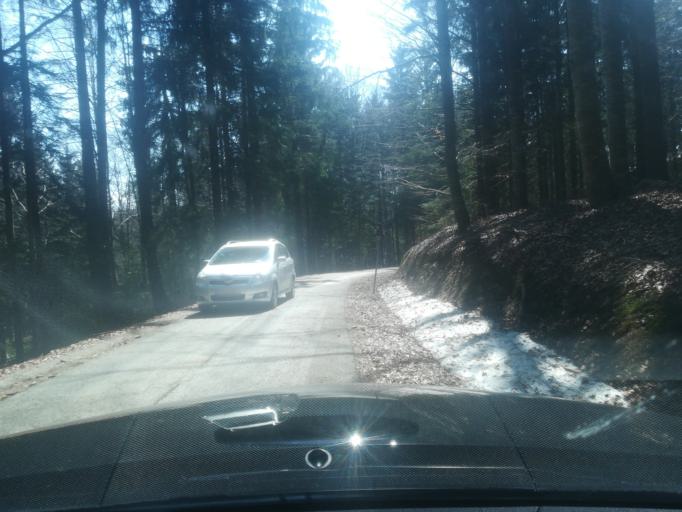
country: AT
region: Lower Austria
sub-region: Politischer Bezirk Zwettl
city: Langschlag
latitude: 48.5017
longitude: 14.8536
